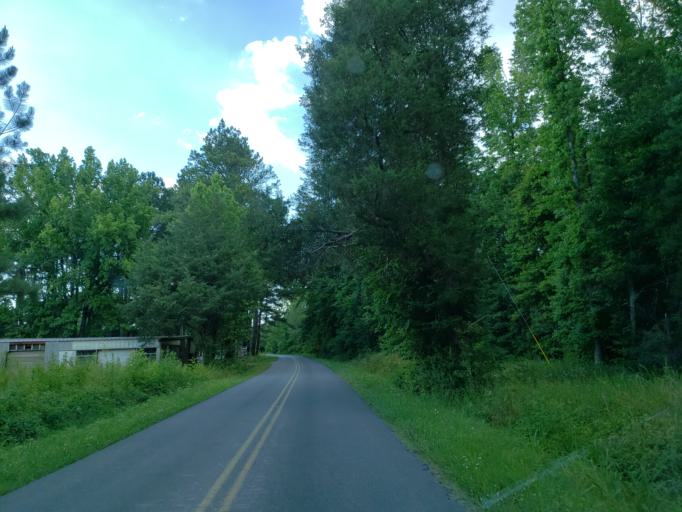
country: US
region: Georgia
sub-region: Polk County
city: Cedartown
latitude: 33.9319
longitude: -85.2711
